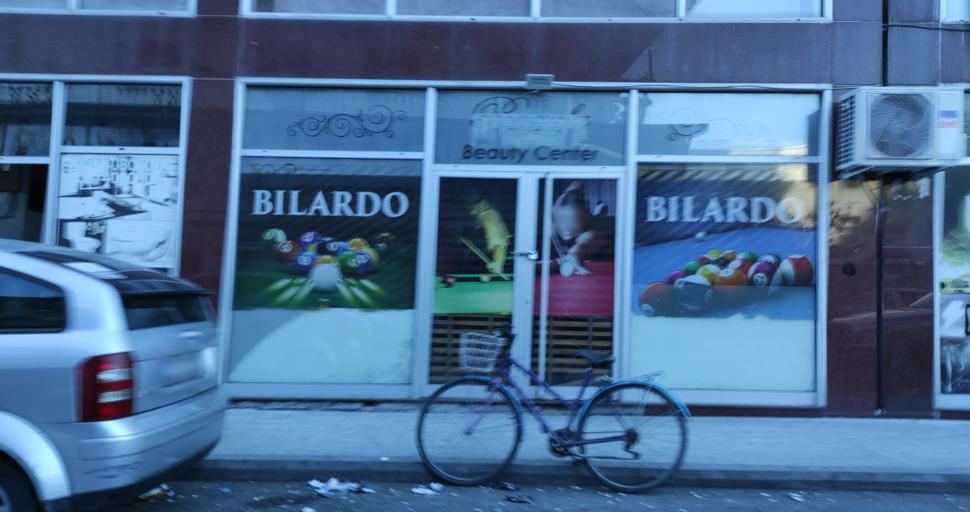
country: AL
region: Shkoder
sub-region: Rrethi i Shkodres
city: Shkoder
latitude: 42.0733
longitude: 19.5095
